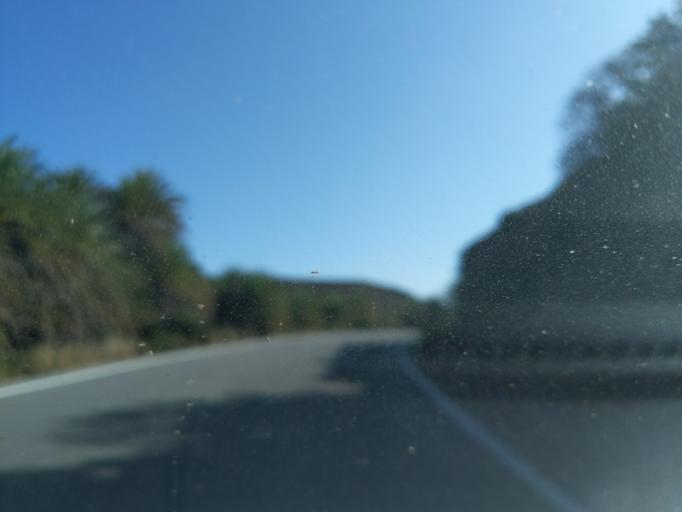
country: GR
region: Crete
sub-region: Nomos Lasithiou
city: Palekastro
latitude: 35.2547
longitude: 26.2584
